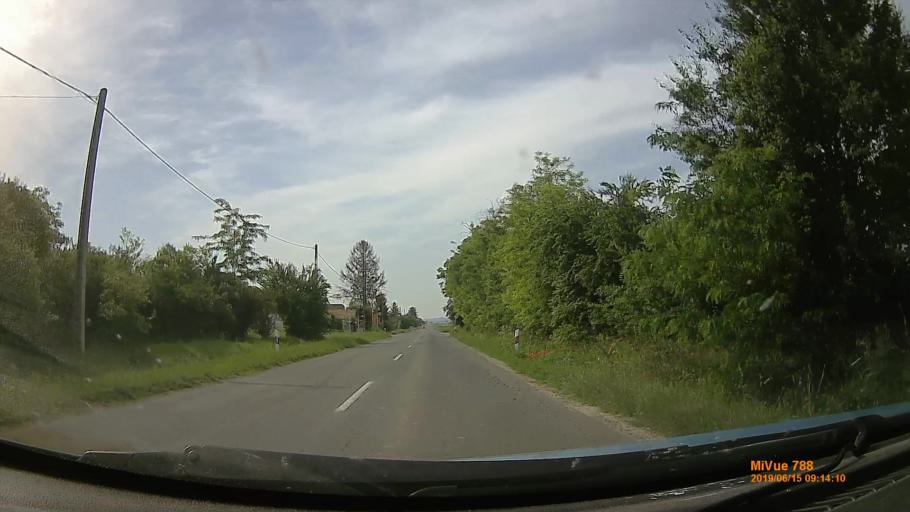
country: HU
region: Tolna
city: Iregszemcse
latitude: 46.6459
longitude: 18.1955
